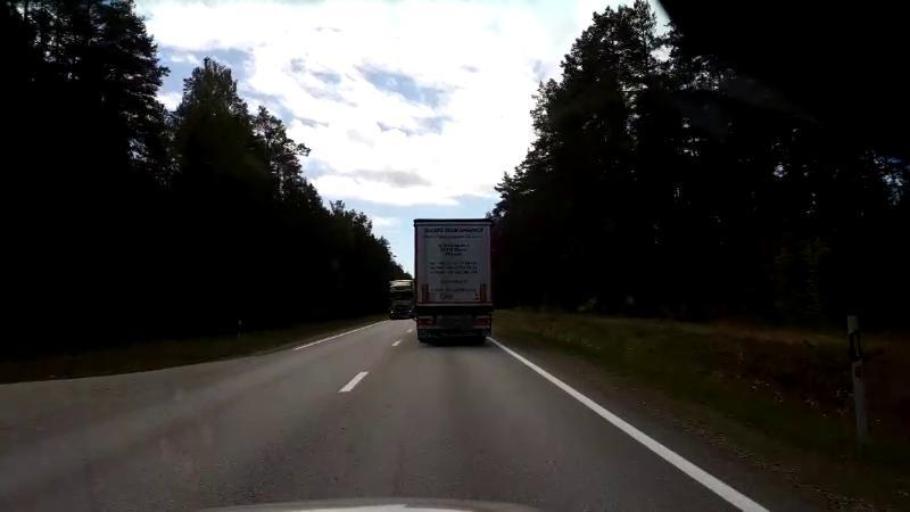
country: LV
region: Salacgrivas
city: Salacgriva
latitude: 57.5193
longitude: 24.4306
